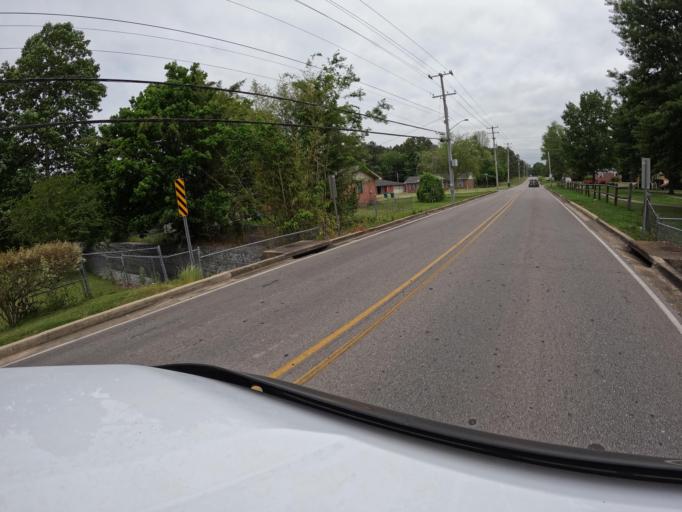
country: US
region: Mississippi
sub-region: Lee County
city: Tupelo
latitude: 34.2674
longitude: -88.7377
